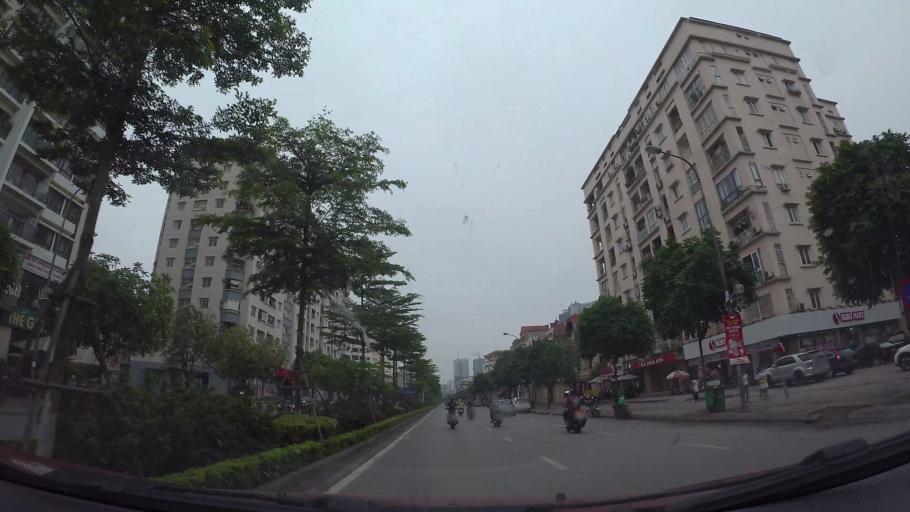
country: VN
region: Ha Noi
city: Cau Giay
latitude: 21.0185
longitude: 105.7929
